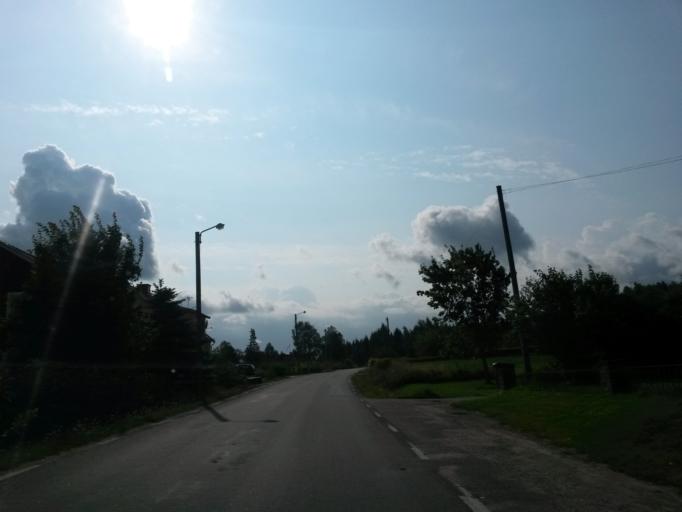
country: SE
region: Vaestra Goetaland
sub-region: Vargarda Kommun
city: Jonstorp
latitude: 58.0080
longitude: 12.7089
